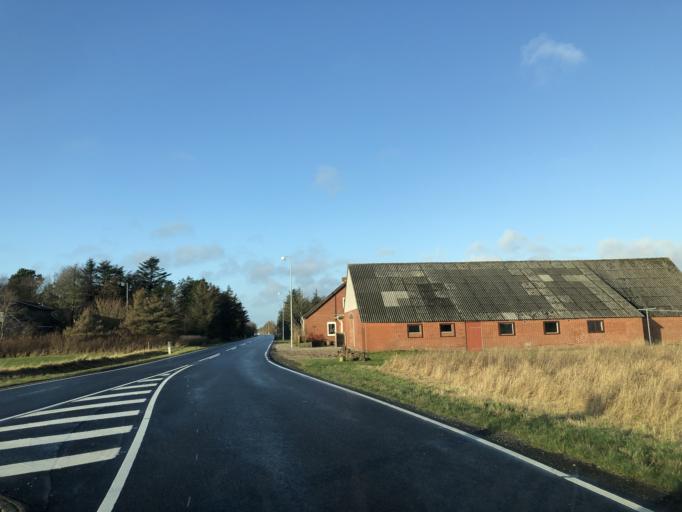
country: DK
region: Central Jutland
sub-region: Struer Kommune
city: Struer
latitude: 56.5448
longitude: 8.4980
